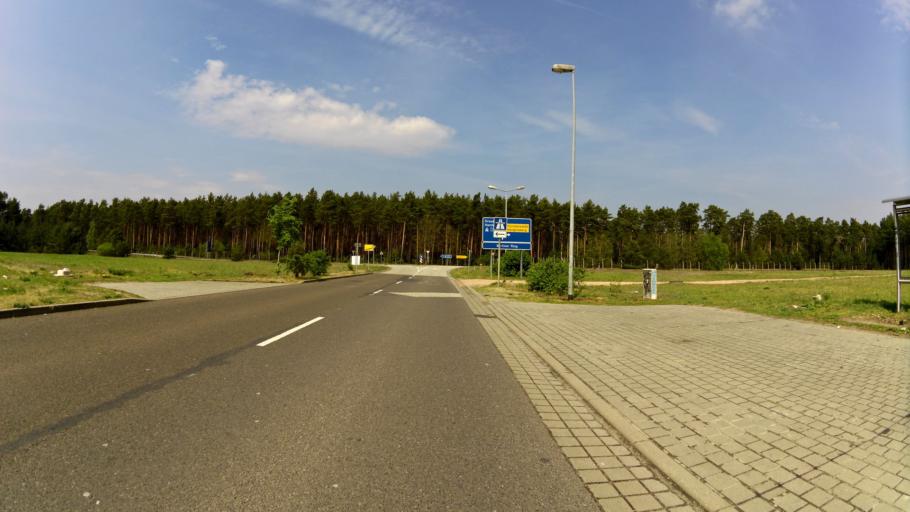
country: DE
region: Brandenburg
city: Grunheide
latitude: 52.3886
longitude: 13.7916
